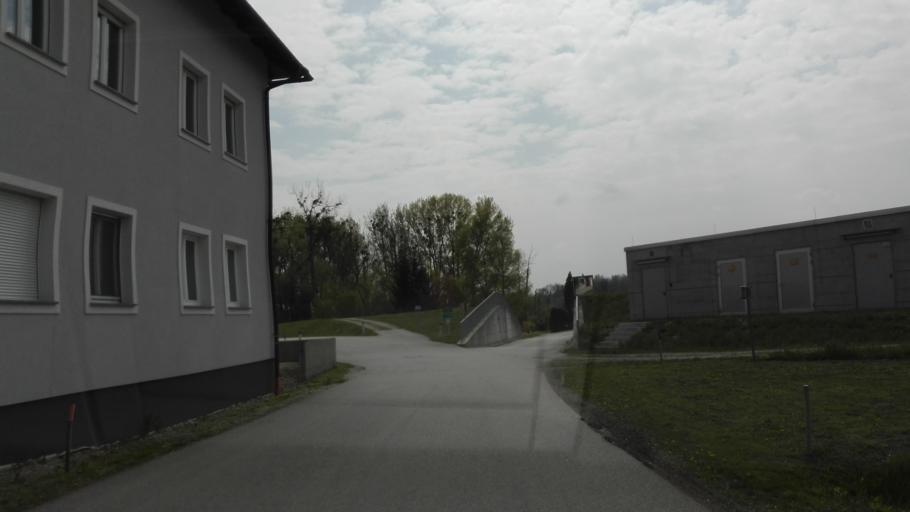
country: AT
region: Upper Austria
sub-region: Politischer Bezirk Perg
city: Perg
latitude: 48.2104
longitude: 14.6175
